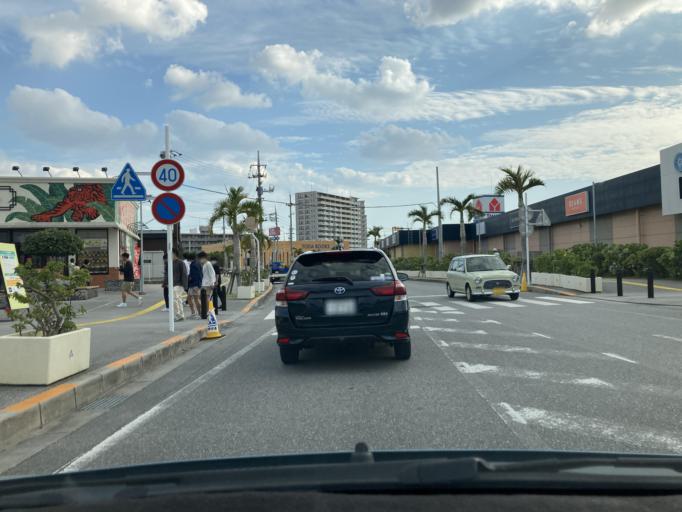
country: JP
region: Okinawa
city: Itoman
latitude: 26.1595
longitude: 127.6580
